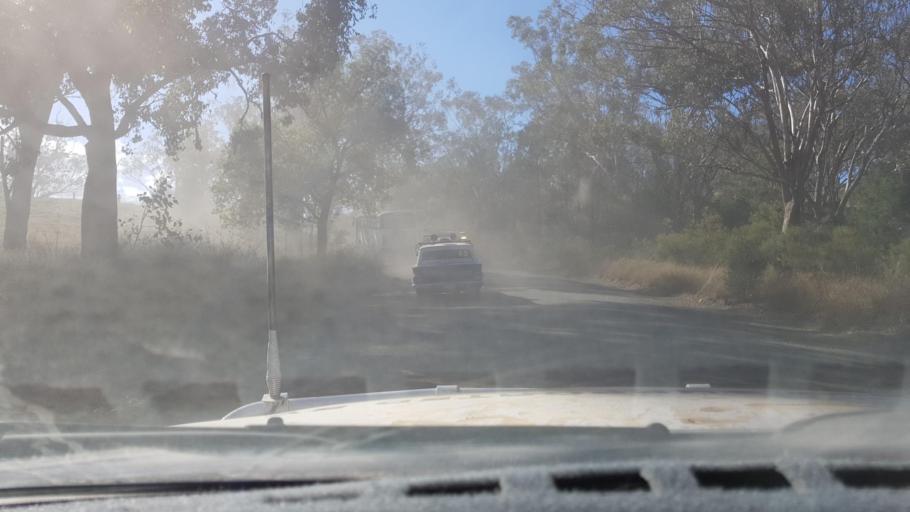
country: AU
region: New South Wales
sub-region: Tamworth Municipality
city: Manilla
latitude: -30.6590
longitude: 150.4765
